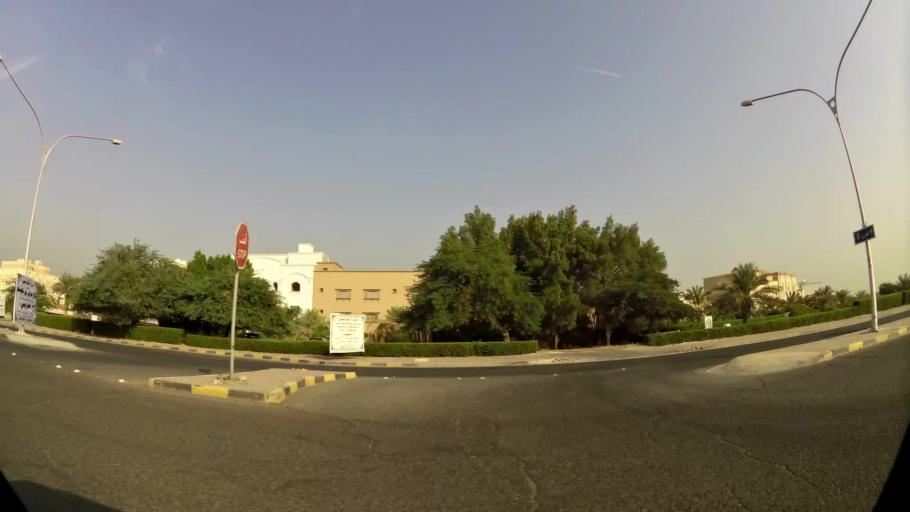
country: KW
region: Al Ahmadi
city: Al Manqaf
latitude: 29.0948
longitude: 48.1061
